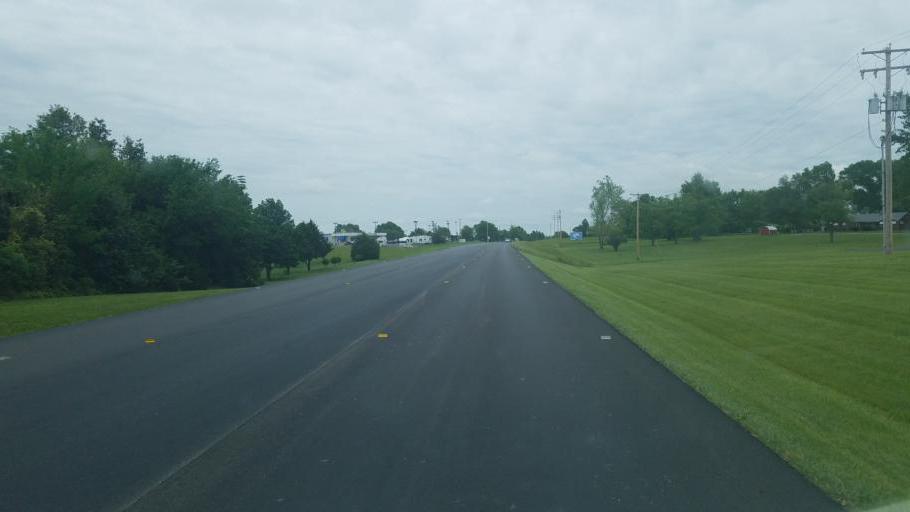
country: US
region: Missouri
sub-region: Morgan County
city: Versailles
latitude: 38.4389
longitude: -92.8446
